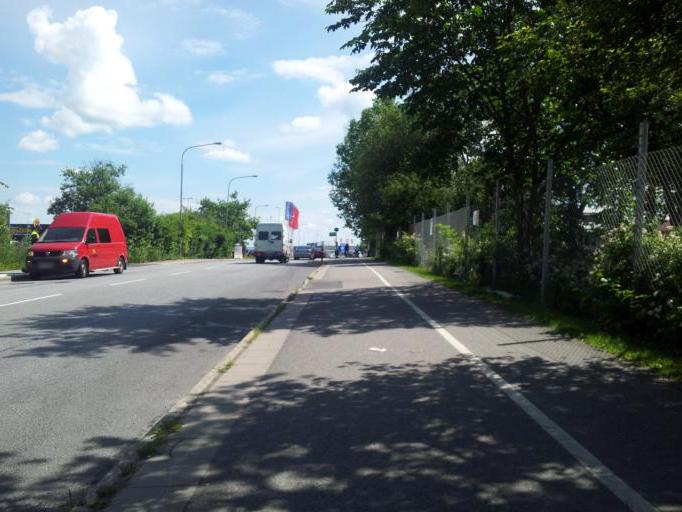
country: SE
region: Uppsala
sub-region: Uppsala Kommun
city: Saevja
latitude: 59.8536
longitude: 17.6800
